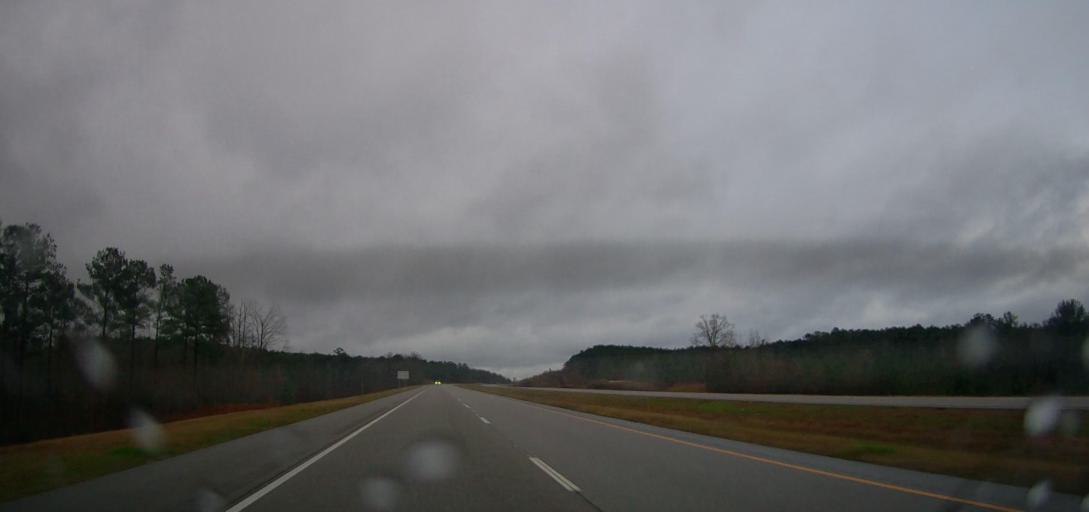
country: US
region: Alabama
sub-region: Bibb County
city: Centreville
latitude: 32.9557
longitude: -87.1210
